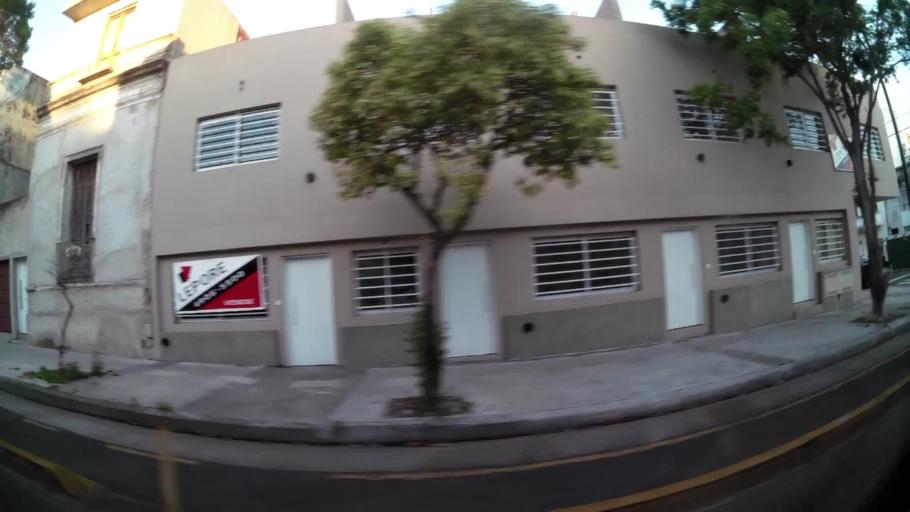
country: AR
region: Buenos Aires F.D.
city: Buenos Aires
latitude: -34.6357
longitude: -58.4209
